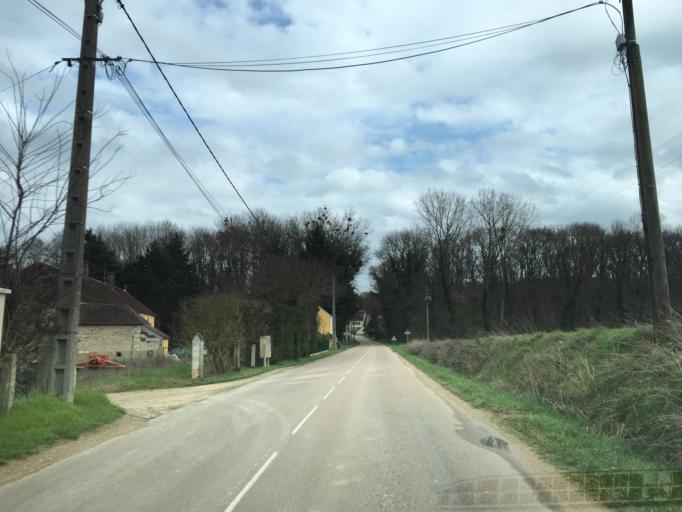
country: FR
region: Bourgogne
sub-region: Departement de l'Yonne
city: Pourrain
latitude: 47.7916
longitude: 3.3946
